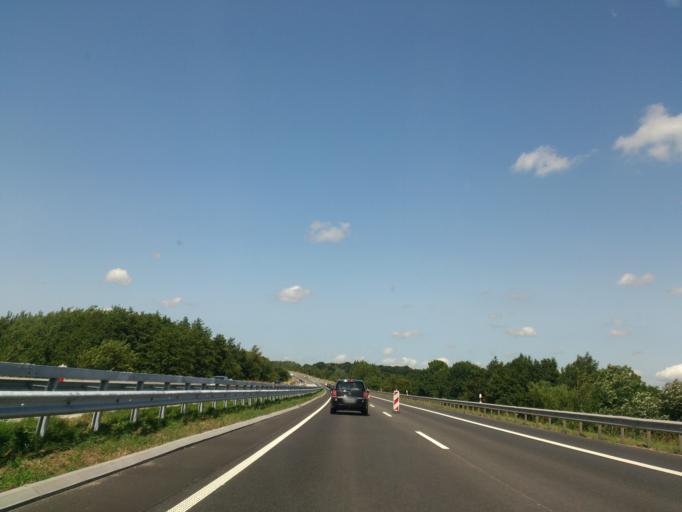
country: DE
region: Schleswig-Holstein
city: Arkebek
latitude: 54.1431
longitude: 9.2468
